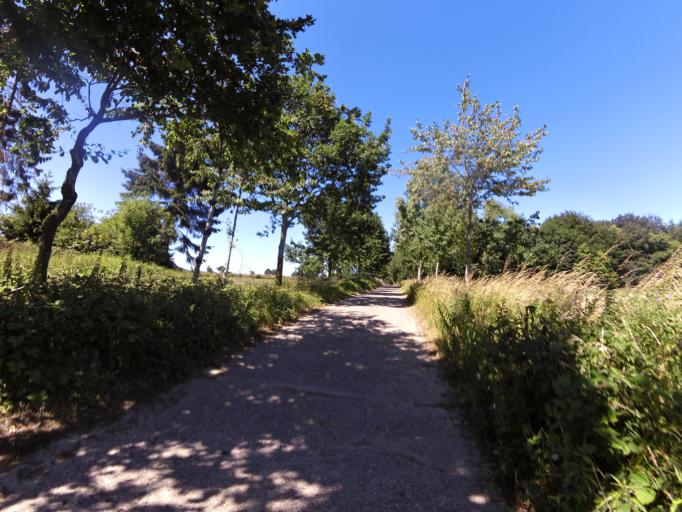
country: BE
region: Flanders
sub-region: Provincie West-Vlaanderen
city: Ichtegem
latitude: 51.0779
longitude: 3.0444
